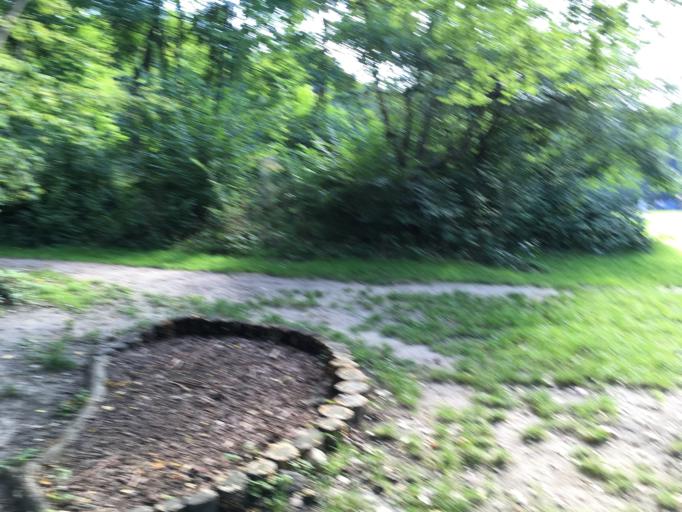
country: PL
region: Pomeranian Voivodeship
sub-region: Gdansk
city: Gdansk
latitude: 54.3753
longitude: 18.5941
